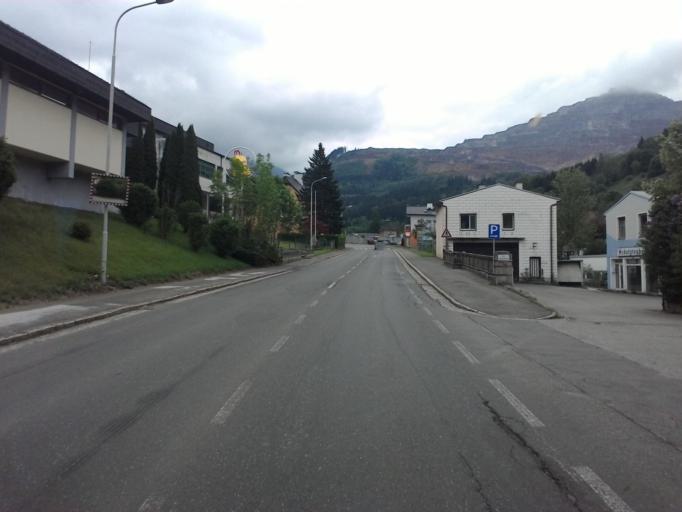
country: AT
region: Styria
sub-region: Politischer Bezirk Leoben
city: Eisenerz
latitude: 47.5425
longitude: 14.8889
